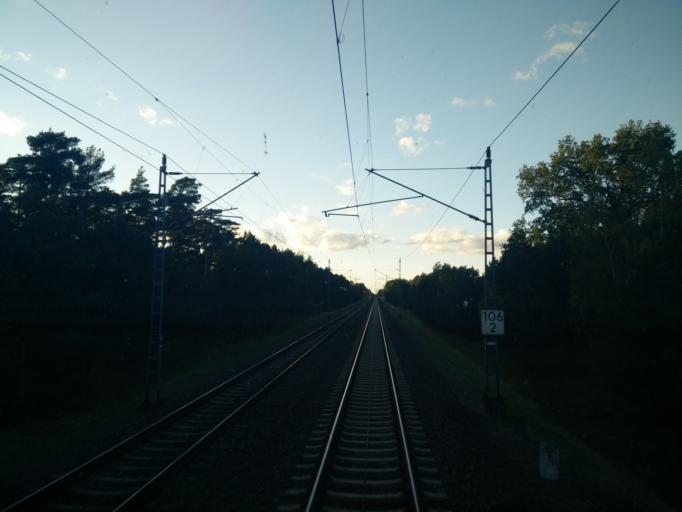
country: DE
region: Brandenburg
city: Plattenburg
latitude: 52.9255
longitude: 12.0300
